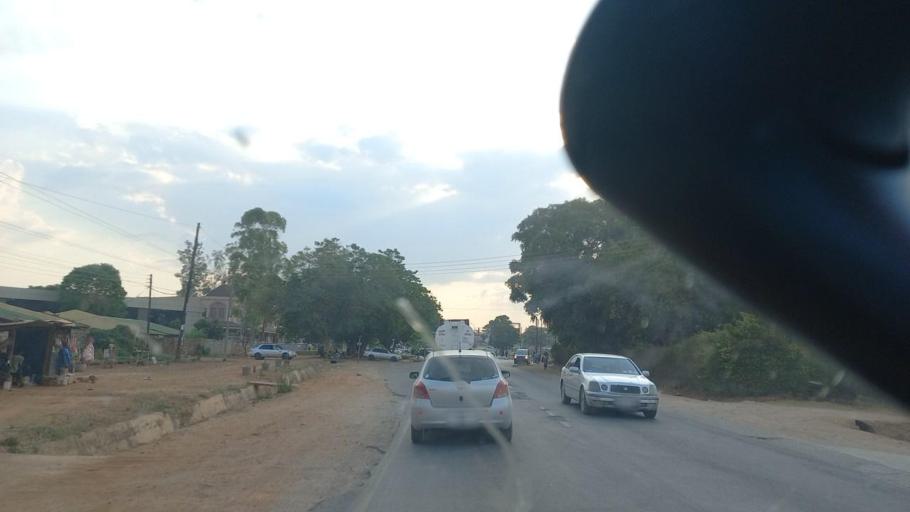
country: ZM
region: Lusaka
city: Lusaka
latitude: -15.3701
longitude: 28.4041
